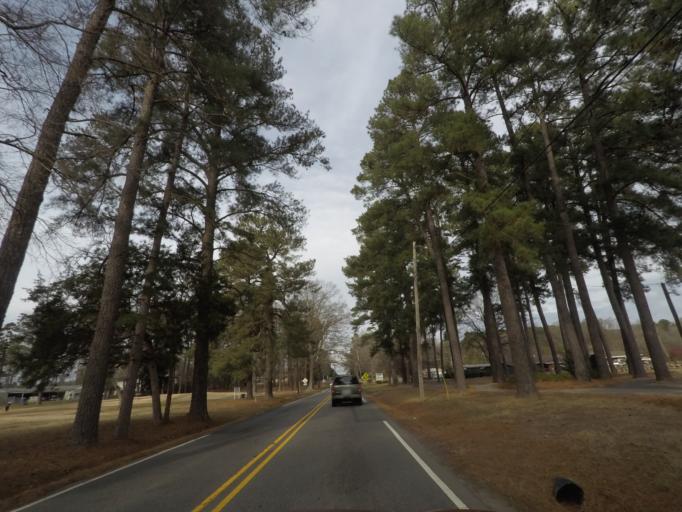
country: US
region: North Carolina
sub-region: Durham County
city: Durham
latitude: 36.0230
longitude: -78.9360
